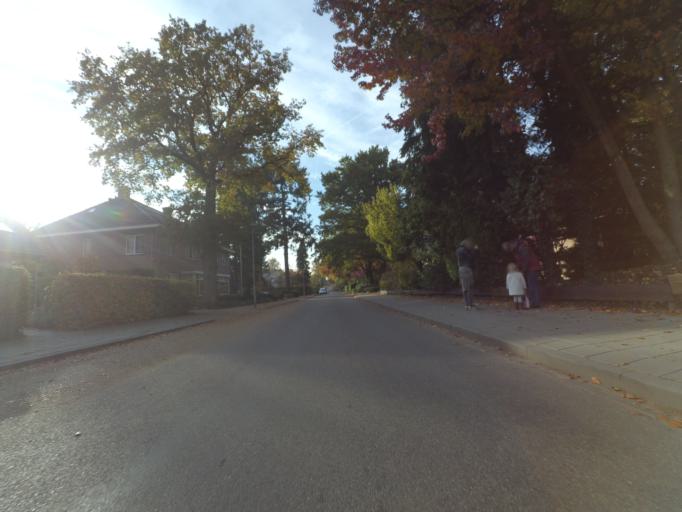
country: NL
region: Gelderland
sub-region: Gemeente Ede
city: Bennekom
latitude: 52.0084
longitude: 5.6844
